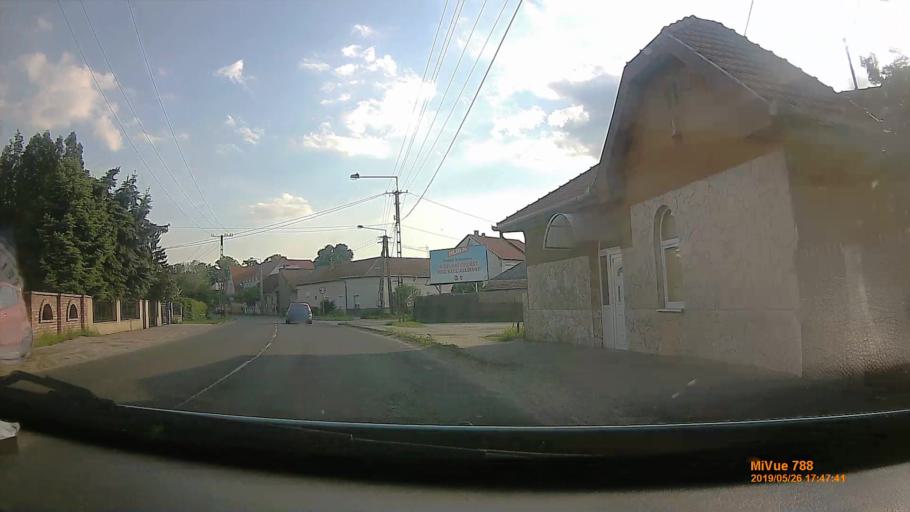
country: HU
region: Borsod-Abauj-Zemplen
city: Szikszo
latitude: 48.2004
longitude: 20.9323
